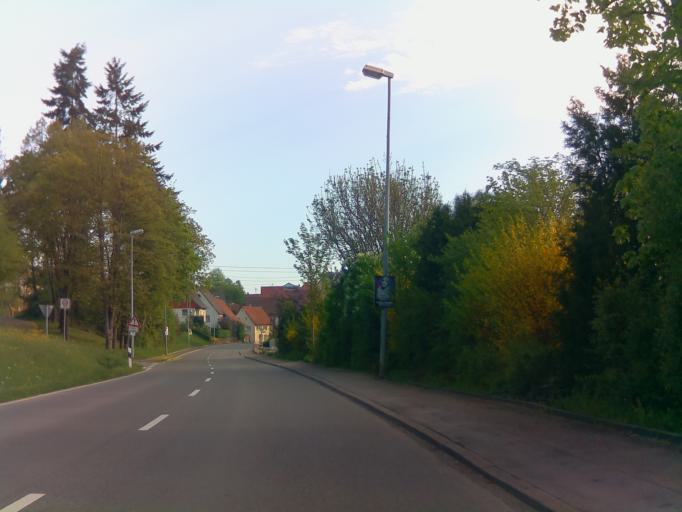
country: DE
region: Baden-Wuerttemberg
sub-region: Tuebingen Region
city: Rosenfeld
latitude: 48.3256
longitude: 8.7259
